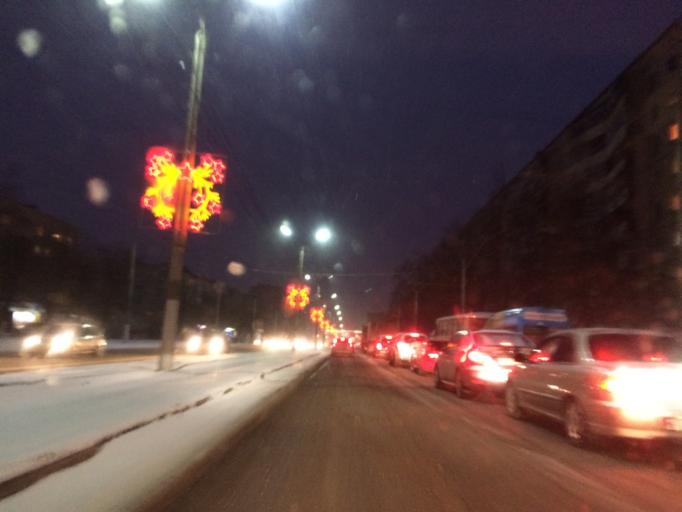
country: RU
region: Tula
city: Tula
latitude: 54.1994
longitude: 37.6505
